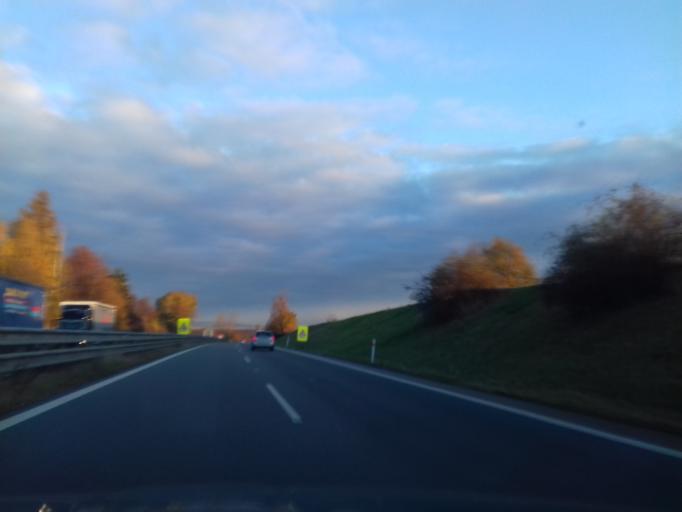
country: CZ
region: Olomoucky
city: Otaslavice
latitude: 49.3815
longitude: 17.0975
